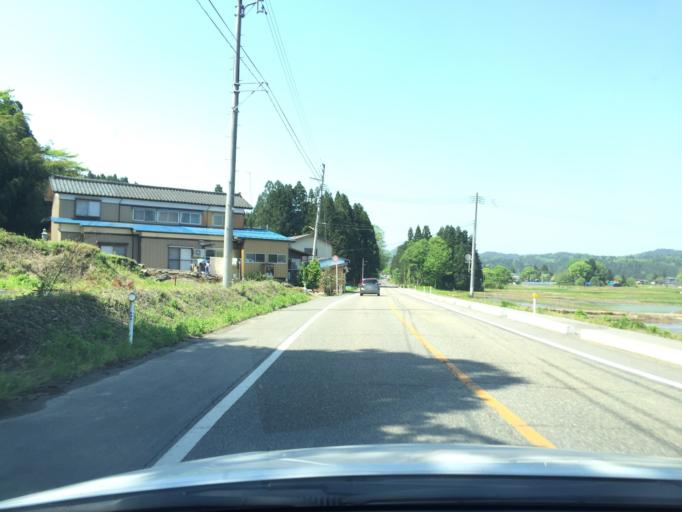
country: JP
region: Niigata
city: Muramatsu
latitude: 37.6693
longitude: 139.1451
